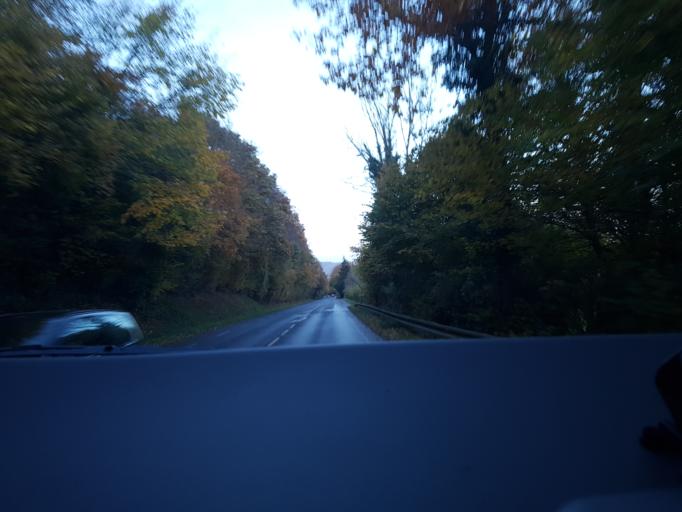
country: FR
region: Lower Normandy
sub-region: Departement du Calvados
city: Saint-Gatien-des-Bois
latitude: 49.2672
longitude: 0.1618
